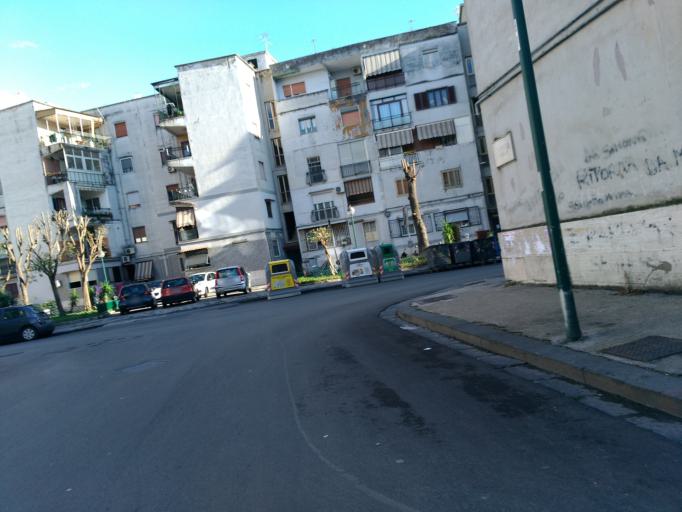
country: IT
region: Campania
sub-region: Provincia di Napoli
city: Arpino
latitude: 40.8580
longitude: 14.2938
